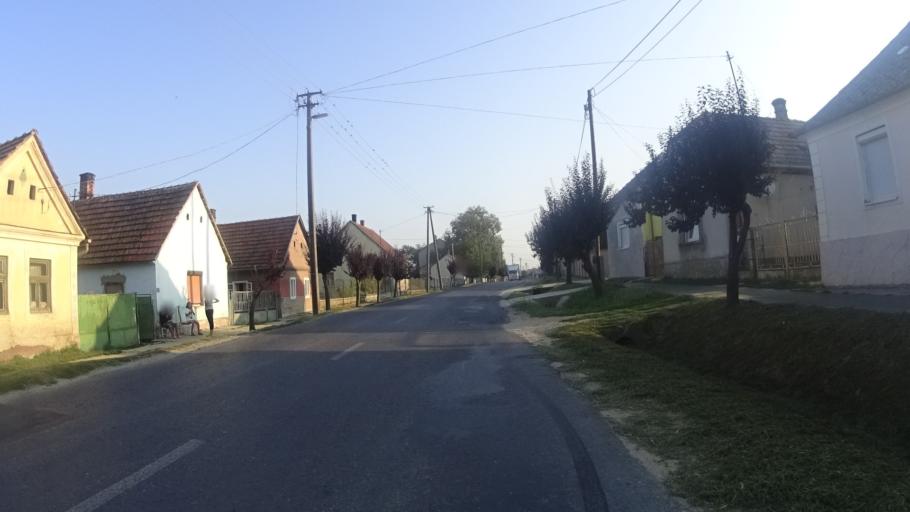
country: HU
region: Zala
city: Zalakomar
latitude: 46.5508
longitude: 17.1745
